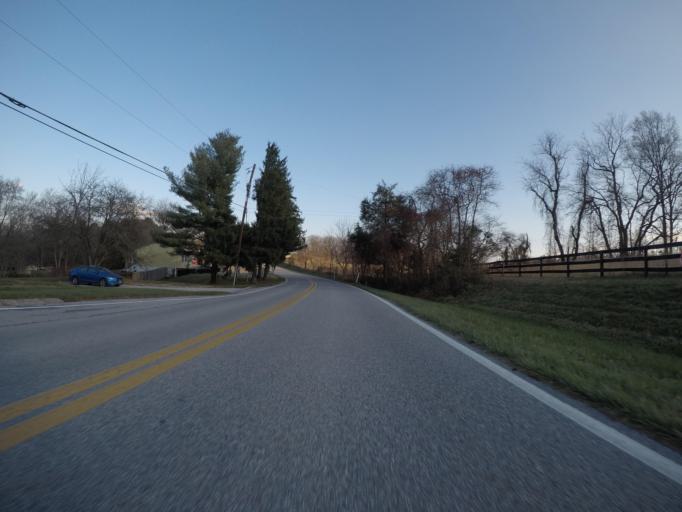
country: US
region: Maryland
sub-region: Carroll County
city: Hampstead
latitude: 39.5723
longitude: -76.9028
